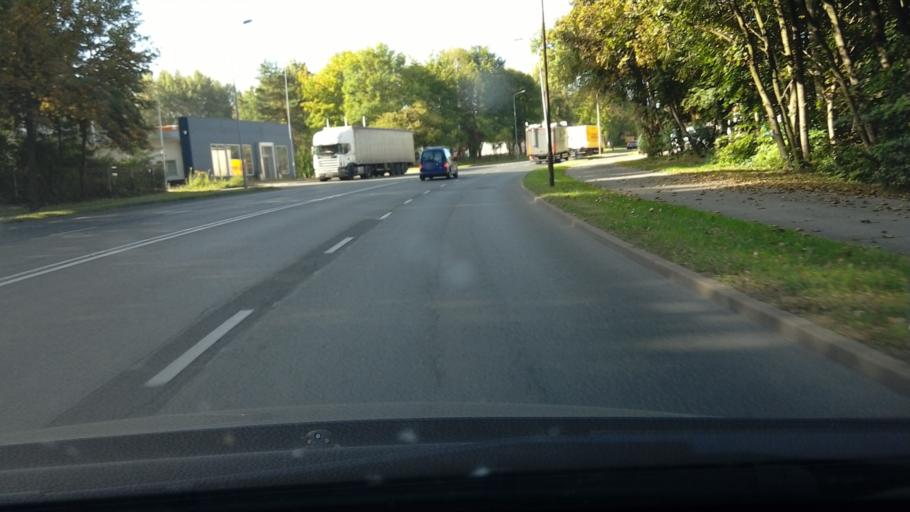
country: PL
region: Lower Silesian Voivodeship
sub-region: Jelenia Gora
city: Jelenia Gora
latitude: 50.8868
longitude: 15.7188
